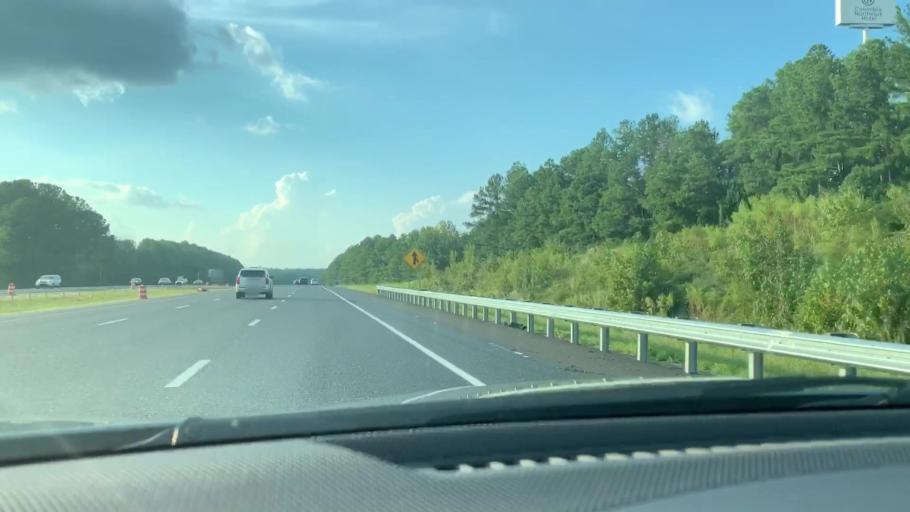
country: US
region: South Carolina
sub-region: Richland County
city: Dentsville
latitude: 34.0830
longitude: -80.9416
